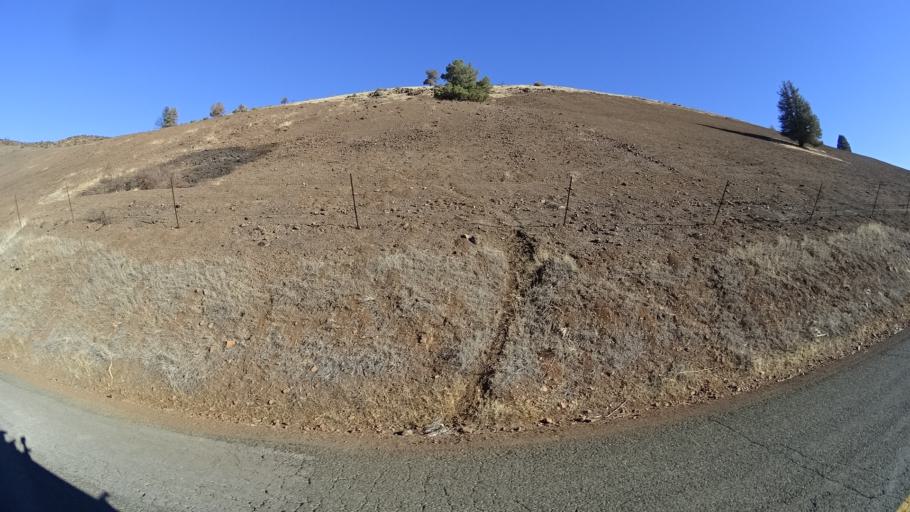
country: US
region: California
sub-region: Siskiyou County
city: Montague
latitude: 41.9057
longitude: -122.4690
